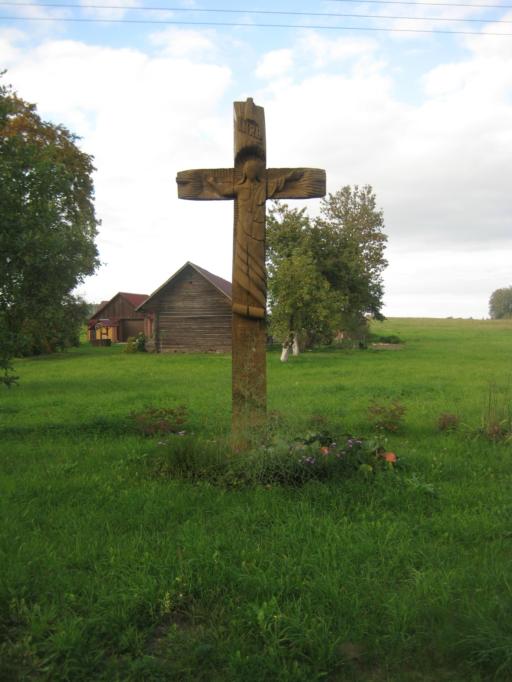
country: LT
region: Utenos apskritis
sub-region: Utena
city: Utena
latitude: 55.6573
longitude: 25.4930
